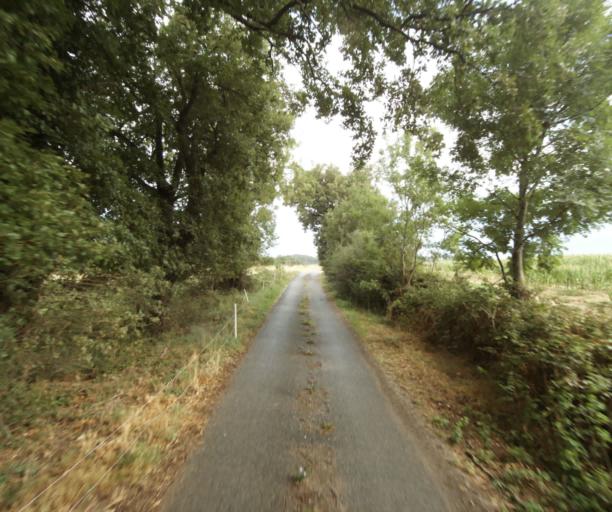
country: FR
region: Midi-Pyrenees
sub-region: Departement de la Haute-Garonne
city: Revel
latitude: 43.4150
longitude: 1.9785
